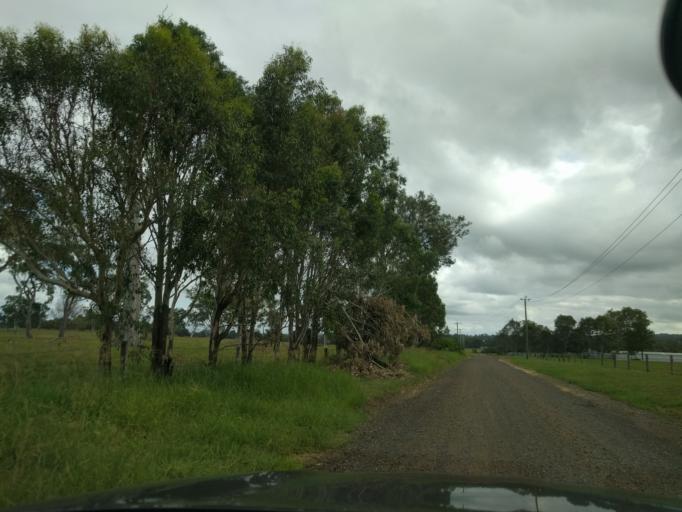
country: AU
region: Queensland
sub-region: Logan
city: Cedar Vale
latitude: -28.0077
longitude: 152.9957
